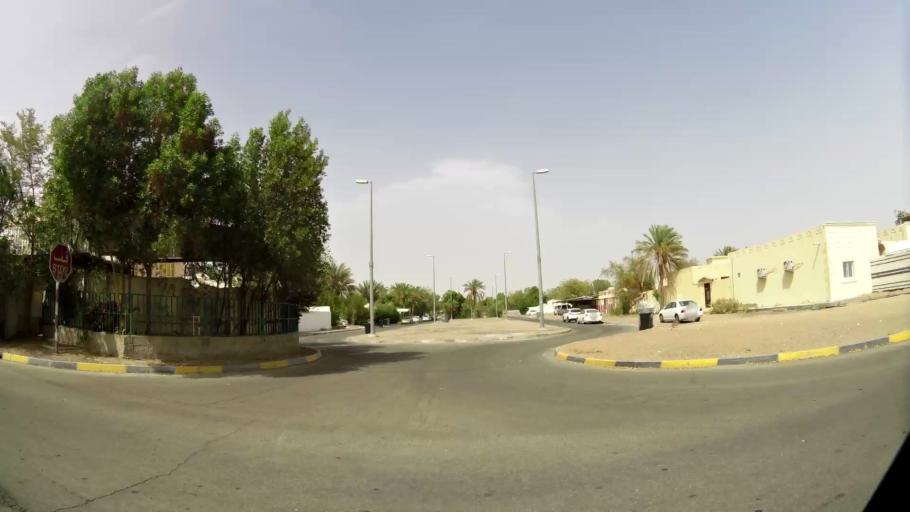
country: AE
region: Abu Dhabi
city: Al Ain
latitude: 24.1921
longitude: 55.6316
